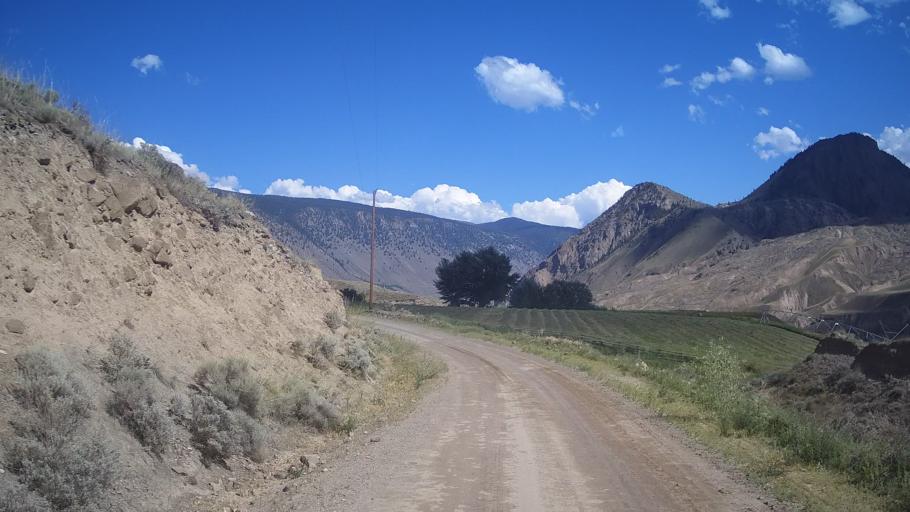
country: CA
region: British Columbia
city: Lillooet
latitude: 51.1810
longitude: -122.1196
